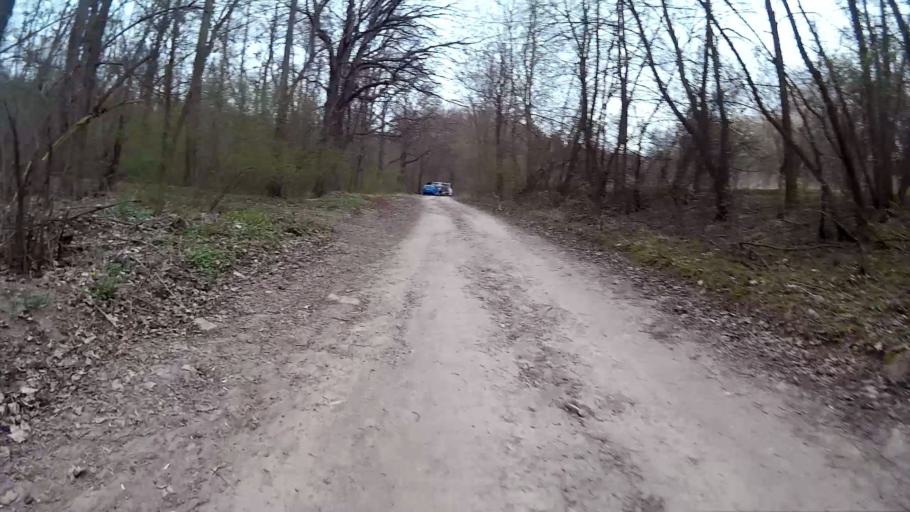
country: CZ
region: South Moravian
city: Ivancice
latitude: 49.0887
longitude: 16.3512
